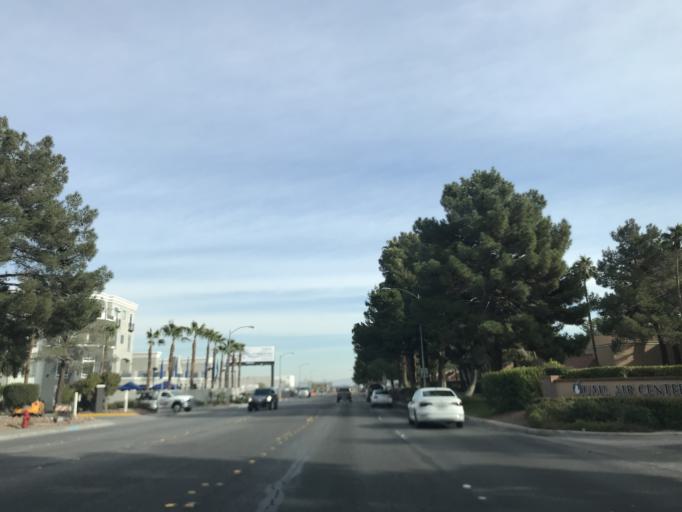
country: US
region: Nevada
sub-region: Clark County
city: Paradise
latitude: 36.0972
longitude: -115.1674
